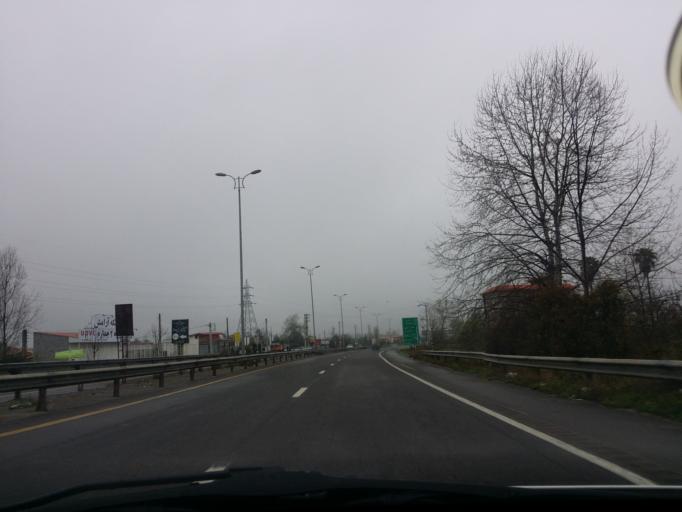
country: IR
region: Mazandaran
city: Tonekabon
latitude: 36.8111
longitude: 50.8581
